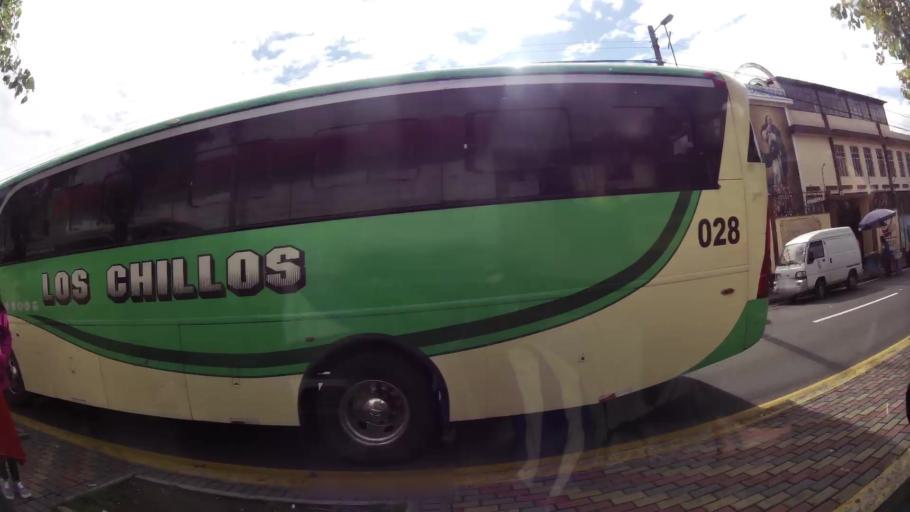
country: EC
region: Pichincha
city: Sangolqui
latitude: -0.3282
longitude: -78.4507
